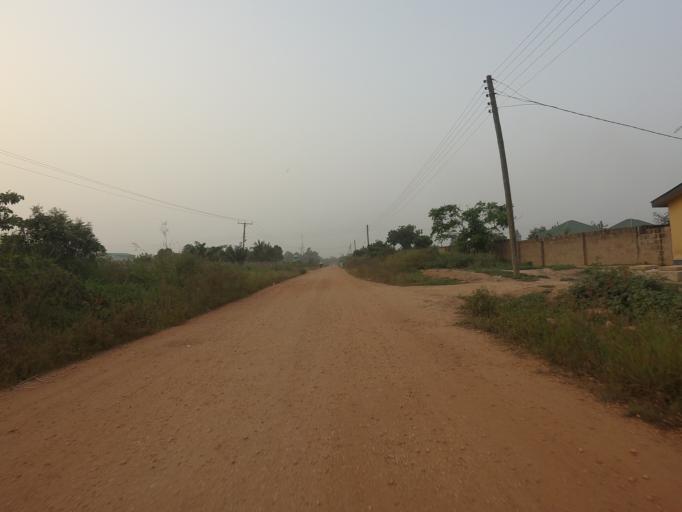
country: GH
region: Volta
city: Anloga
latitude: 5.9869
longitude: 0.5994
